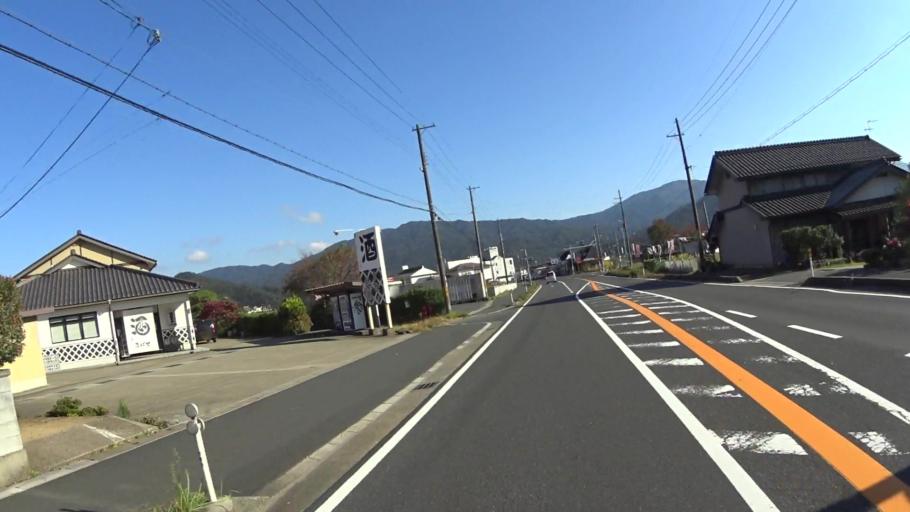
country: JP
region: Kyoto
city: Miyazu
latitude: 35.5374
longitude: 135.1134
